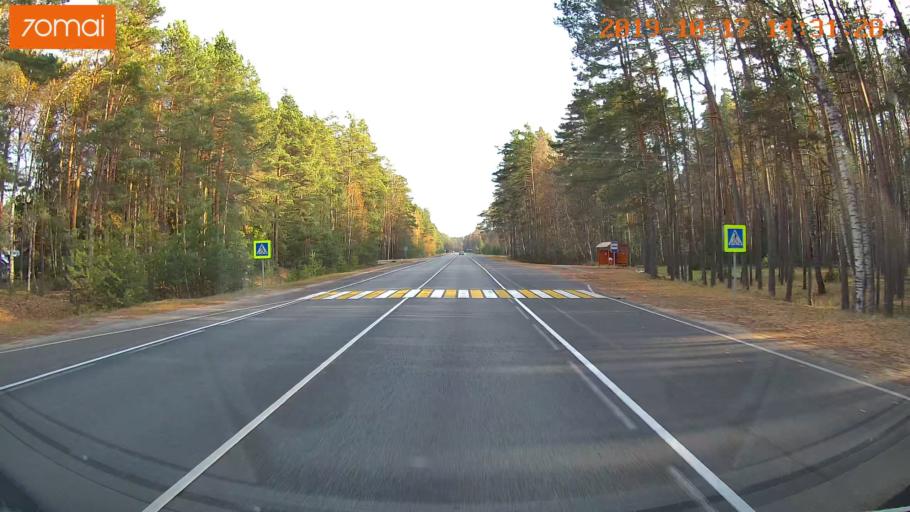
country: RU
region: Rjazan
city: Solotcha
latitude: 54.9364
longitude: 39.9632
